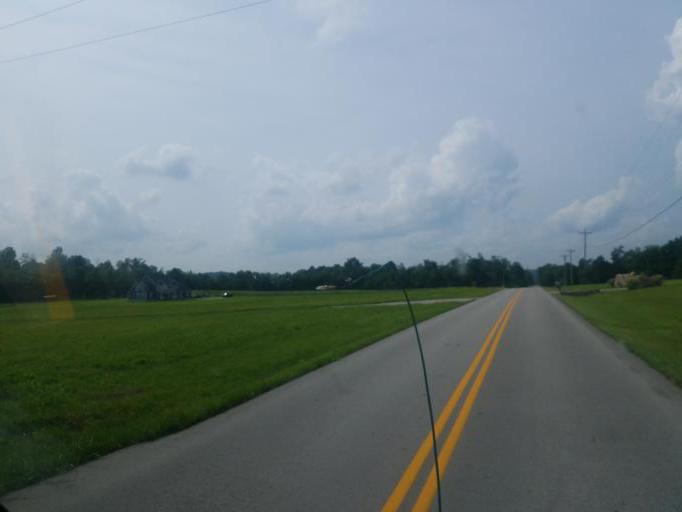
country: US
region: Kentucky
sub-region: Edmonson County
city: Brownsville
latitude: 37.3289
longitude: -86.1225
